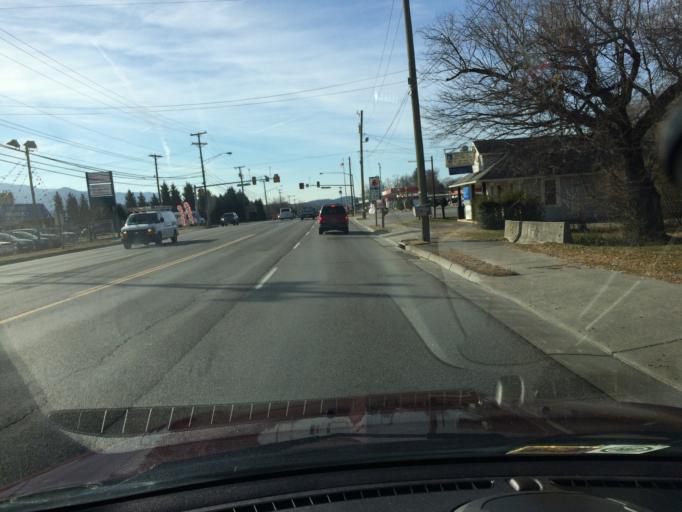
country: US
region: Virginia
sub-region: City of Salem
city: Salem
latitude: 37.2862
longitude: -80.0981
